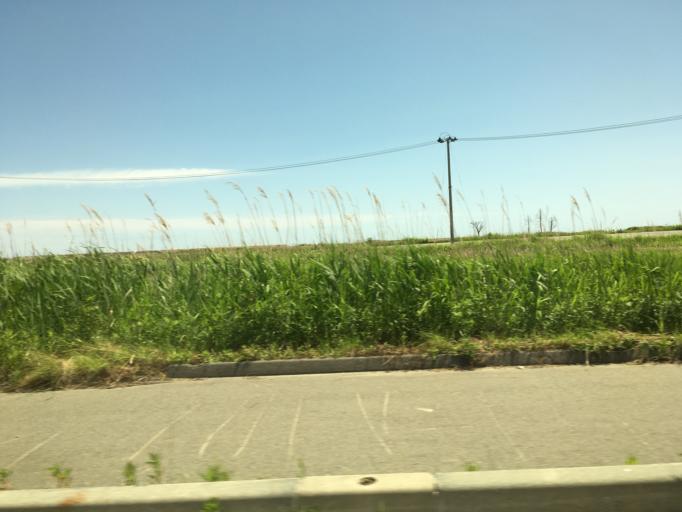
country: JP
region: Fukushima
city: Namie
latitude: 37.4655
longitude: 141.0304
